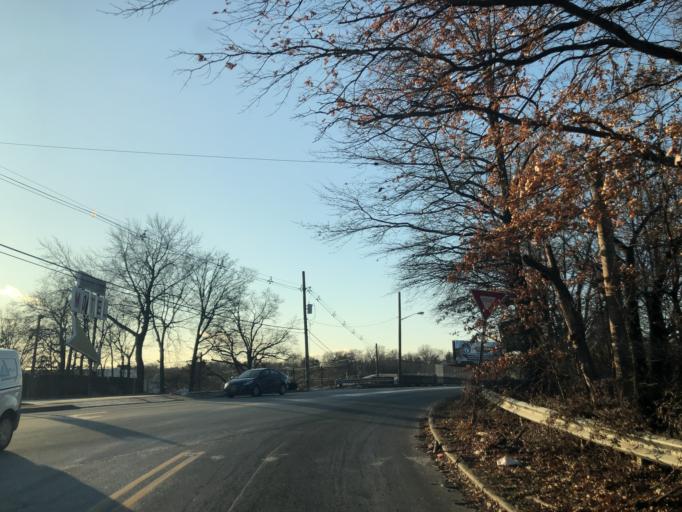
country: US
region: New Jersey
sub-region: Union County
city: Union
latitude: 40.6969
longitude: -74.2520
